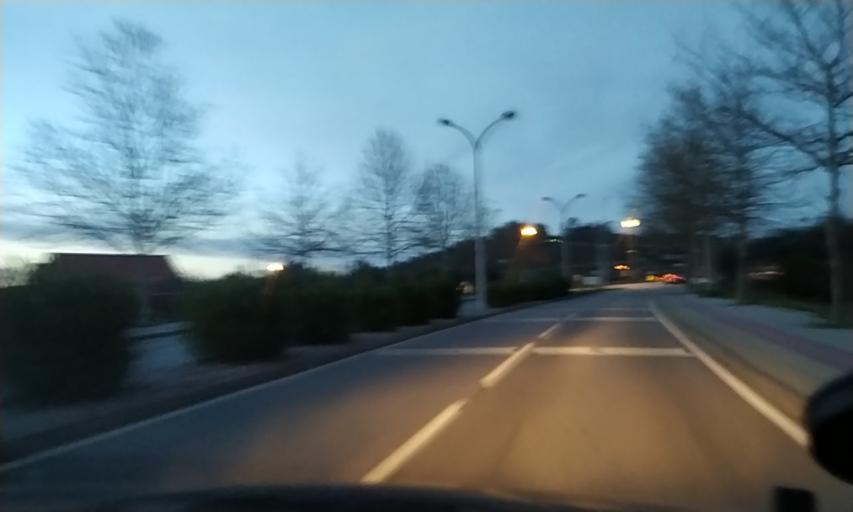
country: PT
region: Castelo Branco
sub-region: Castelo Branco
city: Castelo Branco
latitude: 39.8250
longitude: -7.5101
